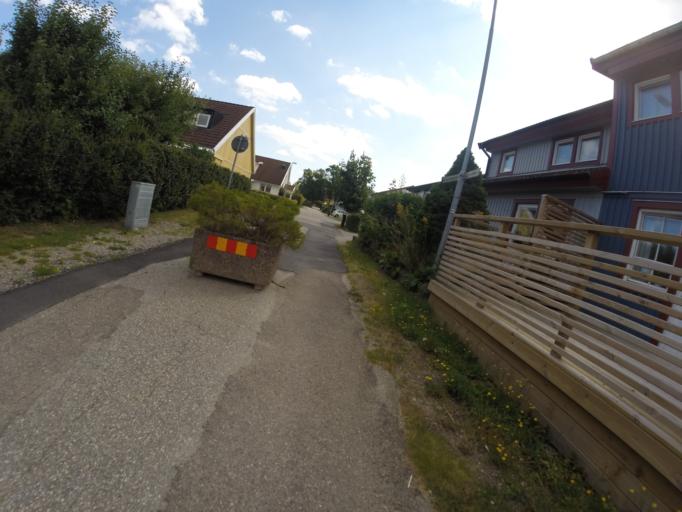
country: SE
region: Soedermanland
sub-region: Eskilstuna Kommun
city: Torshalla
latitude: 59.4079
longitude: 16.4907
